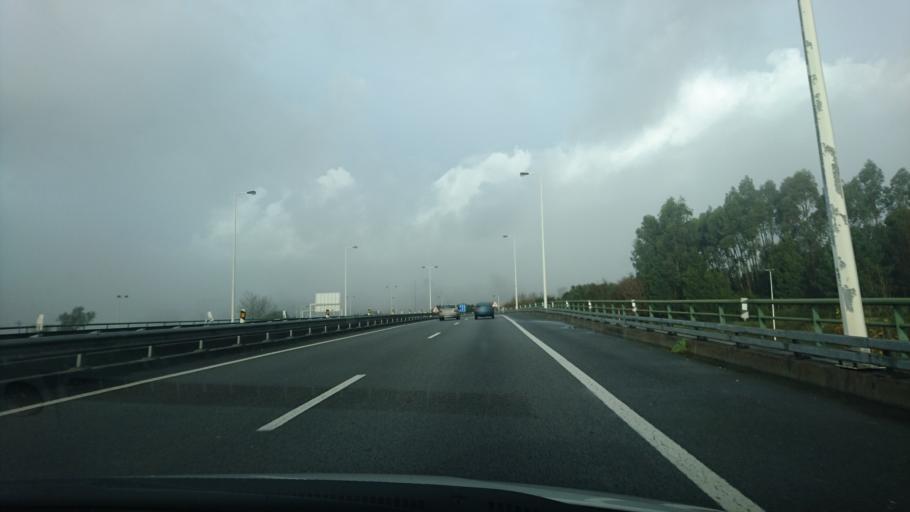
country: PT
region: Porto
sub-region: Gondomar
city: Rio Tinto
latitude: 41.1580
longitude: -8.5610
